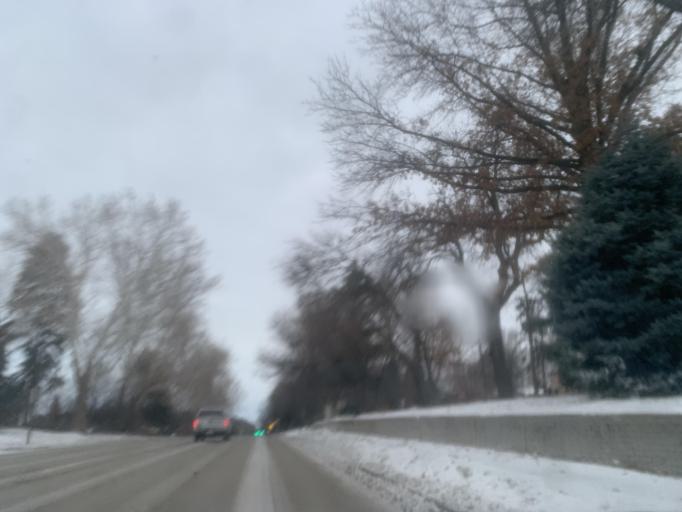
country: US
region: Nebraska
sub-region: Douglas County
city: Ralston
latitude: 41.2589
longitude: -96.0526
